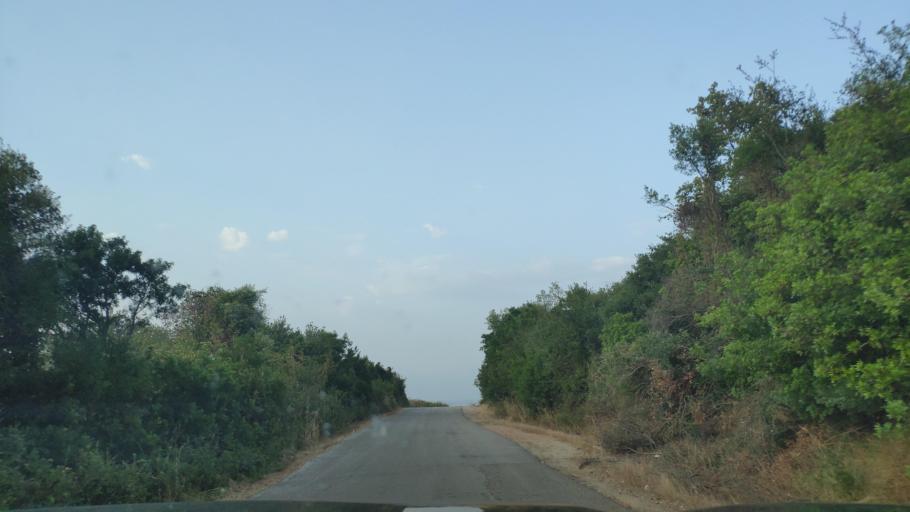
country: GR
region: West Greece
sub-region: Nomos Aitolias kai Akarnanias
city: Monastirakion
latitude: 38.9178
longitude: 20.9764
